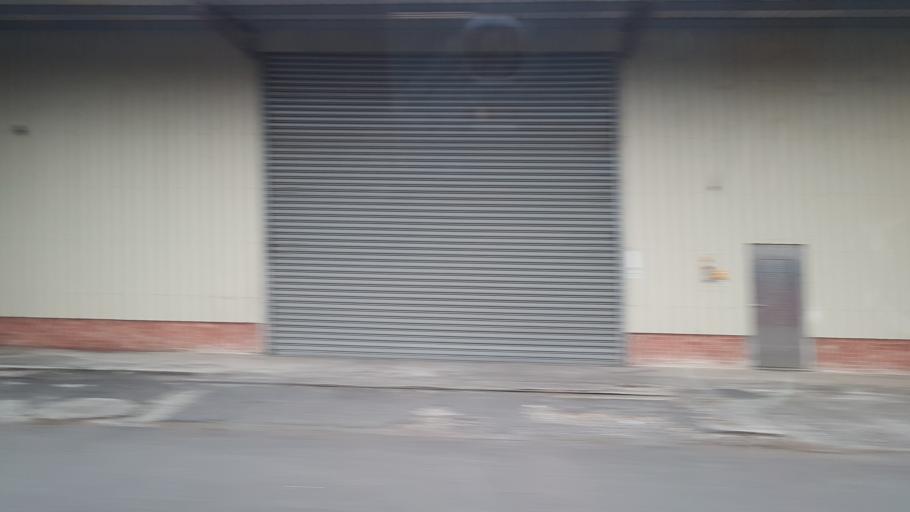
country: TW
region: Taiwan
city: Xinying
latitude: 23.3233
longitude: 120.3161
